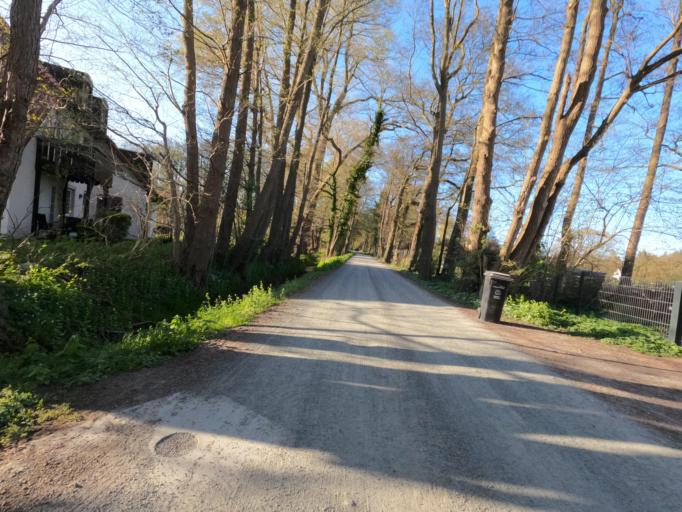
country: DE
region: Mecklenburg-Vorpommern
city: Ostseebad Prerow
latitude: 54.4426
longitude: 12.5519
